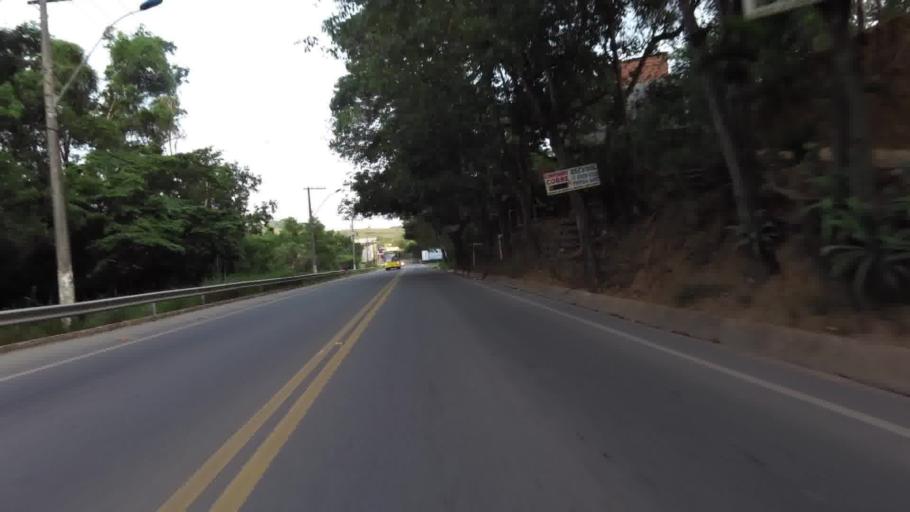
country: BR
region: Espirito Santo
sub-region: Piuma
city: Piuma
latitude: -20.8323
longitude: -40.7251
